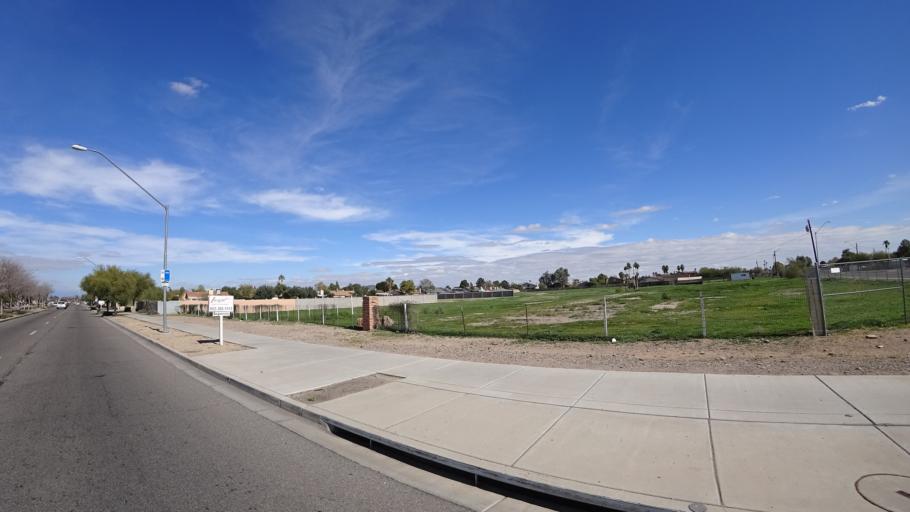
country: US
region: Arizona
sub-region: Maricopa County
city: Peoria
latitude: 33.6324
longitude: -112.2024
